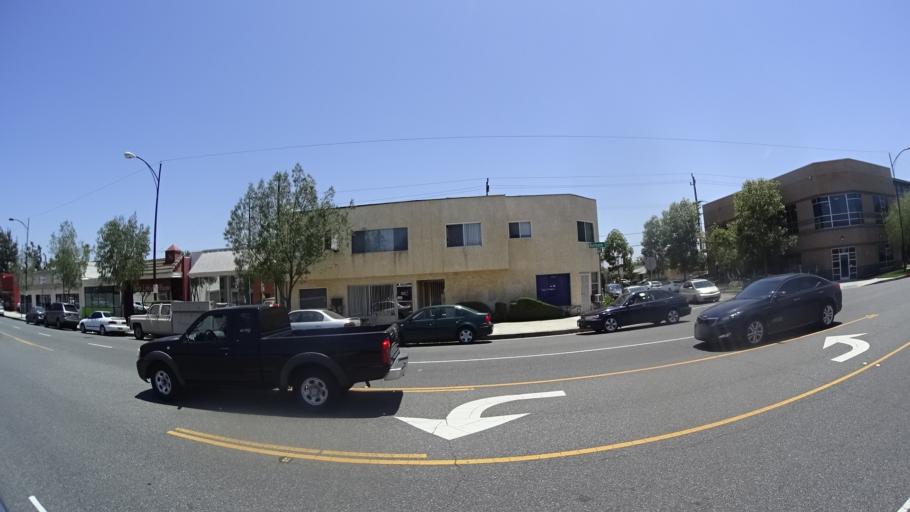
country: US
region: California
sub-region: Los Angeles County
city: North Hollywood
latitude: 34.1755
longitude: -118.3481
